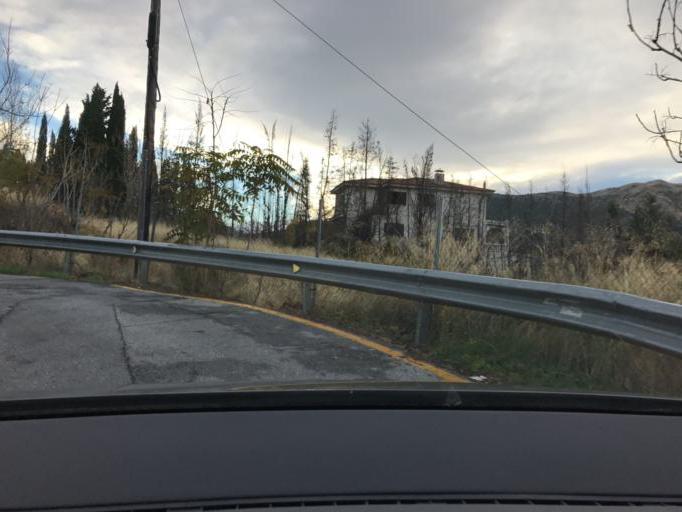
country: ES
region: Andalusia
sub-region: Provincia de Granada
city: Cenes de la Vega
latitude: 37.1620
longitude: -3.5394
